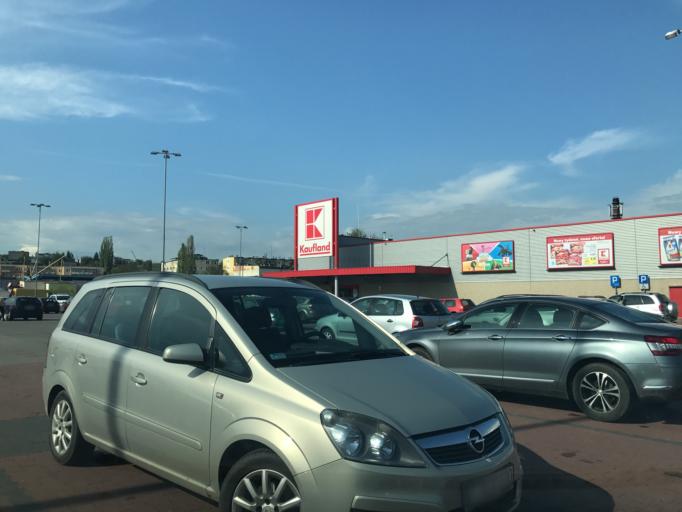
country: PL
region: Kujawsko-Pomorskie
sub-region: Powiat swiecki
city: Swiecie
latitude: 53.4063
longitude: 18.4395
